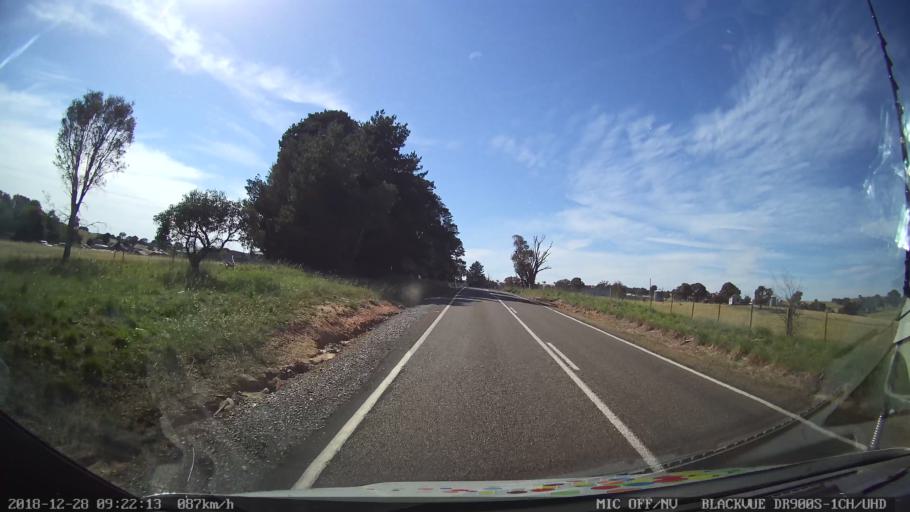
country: AU
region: New South Wales
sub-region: Upper Lachlan Shire
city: Crookwell
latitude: -34.3713
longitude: 149.3801
